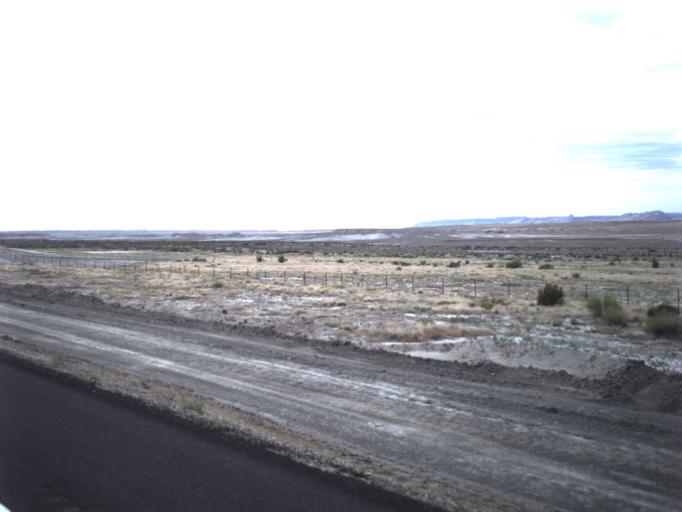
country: US
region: Utah
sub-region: Carbon County
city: East Carbon City
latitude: 39.0511
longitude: -110.3104
